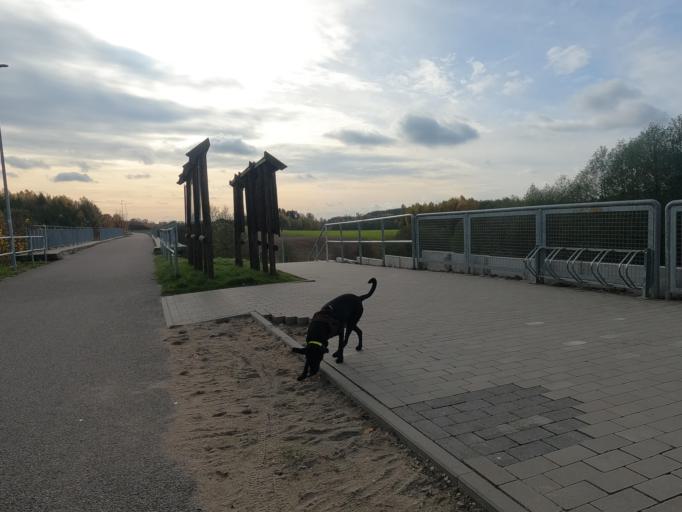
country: PL
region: Pomeranian Voivodeship
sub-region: Powiat starogardzki
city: Starogard Gdanski
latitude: 53.9859
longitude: 18.4708
